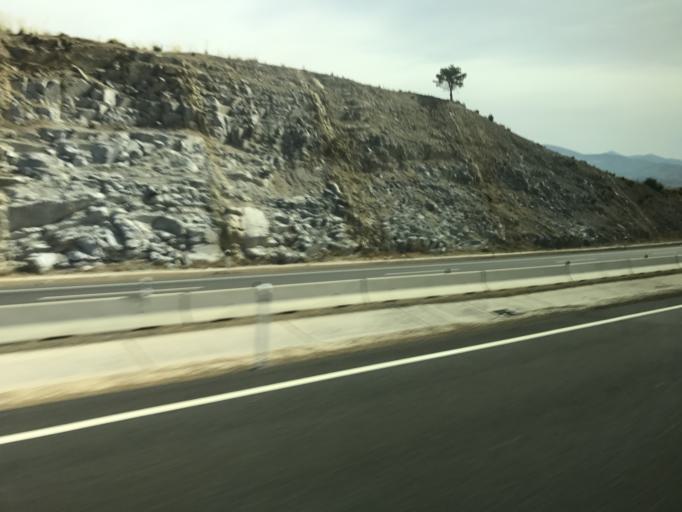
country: ES
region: Castille and Leon
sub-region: Provincia de Segovia
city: Vegas de Matute
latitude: 40.7372
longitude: -4.2684
